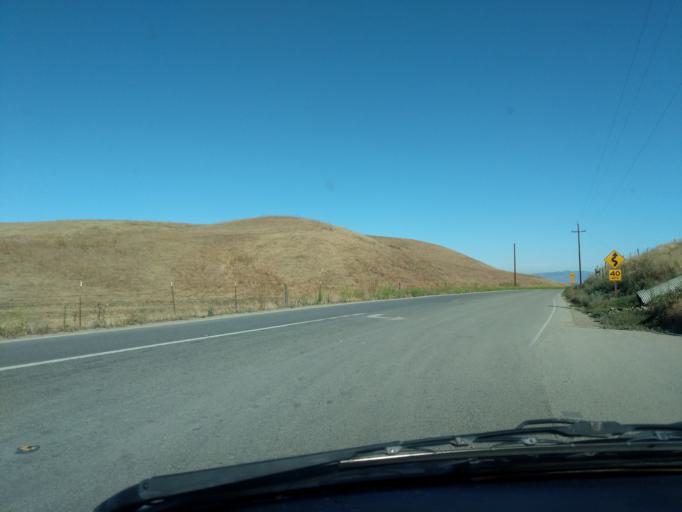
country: US
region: California
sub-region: San Benito County
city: Ridgemark
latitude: 36.8241
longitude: -121.3286
